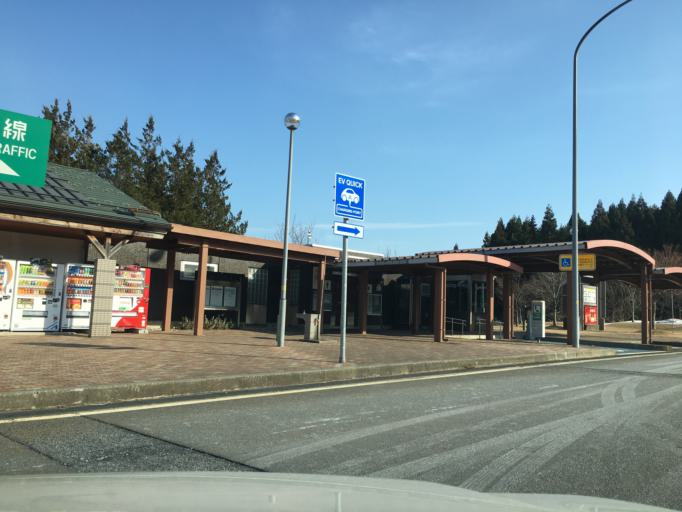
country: JP
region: Yamagata
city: Tsuruoka
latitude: 38.6430
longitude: 139.8301
